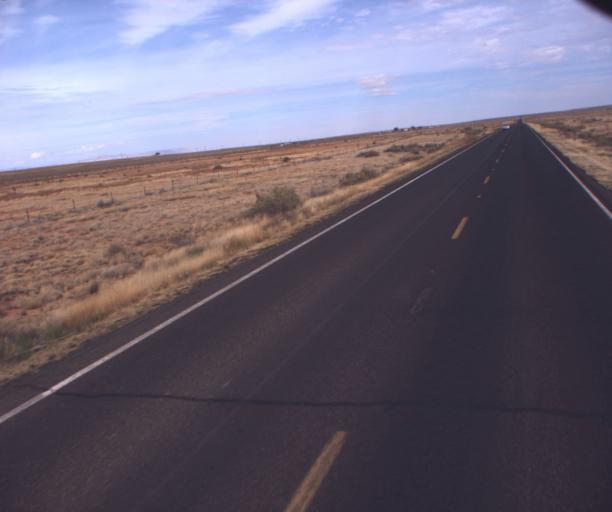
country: US
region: Arizona
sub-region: Apache County
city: Ganado
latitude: 35.7941
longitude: -109.6155
